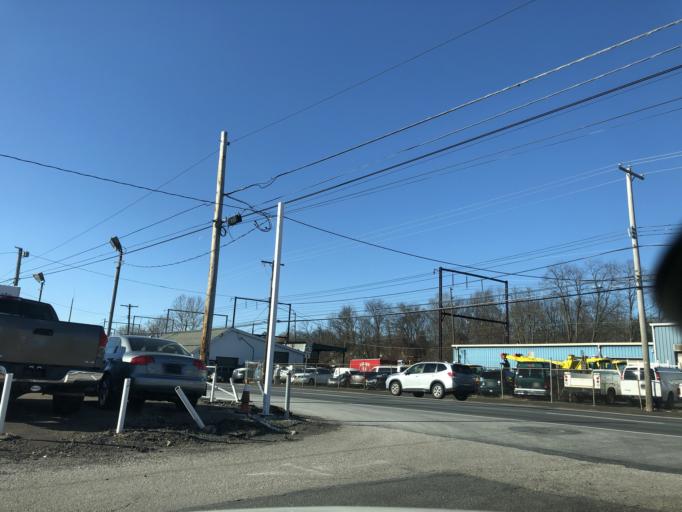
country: US
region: Pennsylvania
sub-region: Bucks County
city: Langhorne Manor
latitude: 40.1619
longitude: -74.9079
